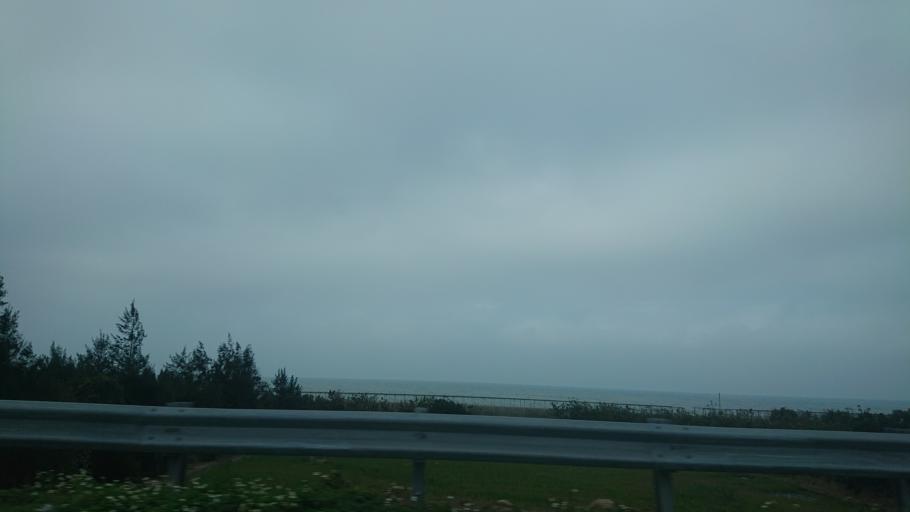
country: TW
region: Taiwan
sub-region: Miaoli
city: Miaoli
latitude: 24.5239
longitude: 120.6885
